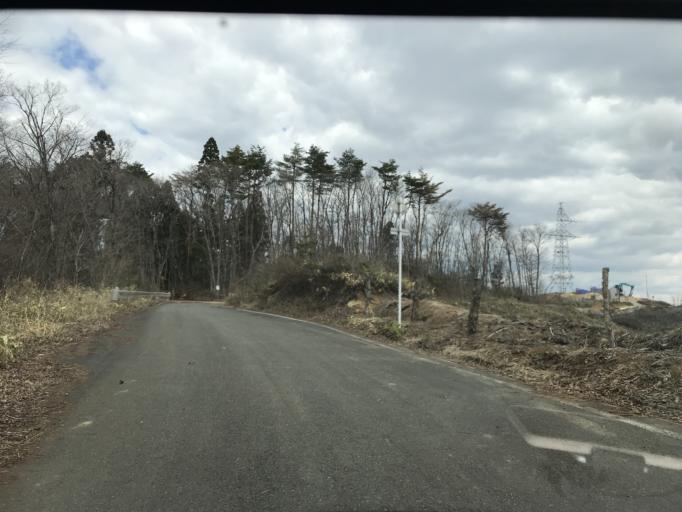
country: JP
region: Iwate
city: Ichinoseki
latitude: 38.9529
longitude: 141.0708
